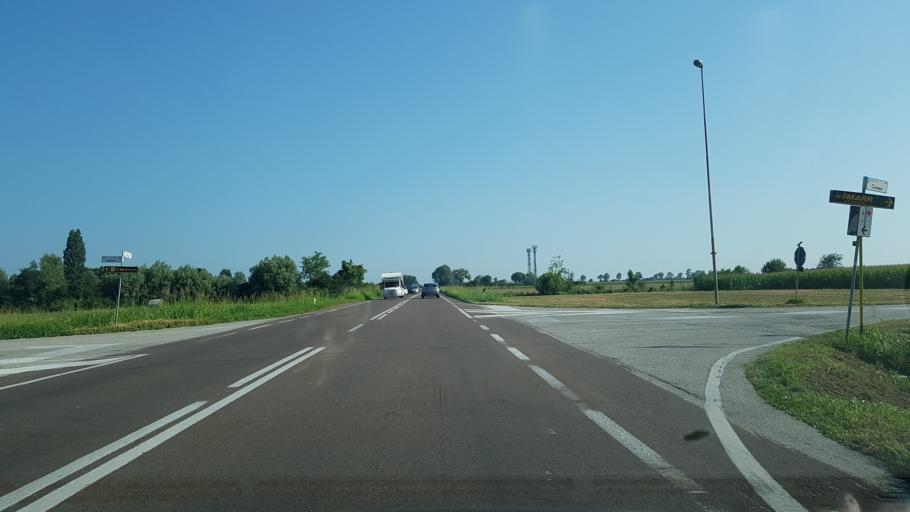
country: IT
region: Veneto
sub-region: Provincia di Venezia
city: San Michele al Tagliamento
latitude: 45.7614
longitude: 12.9858
